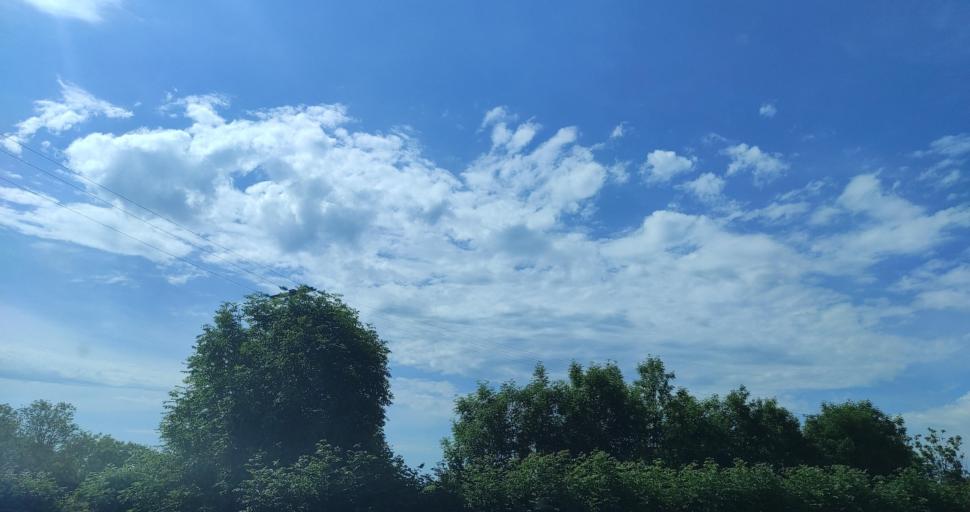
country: FR
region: Midi-Pyrenees
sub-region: Departement de l'Aveyron
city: Laguiole
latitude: 44.6623
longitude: 2.8499
